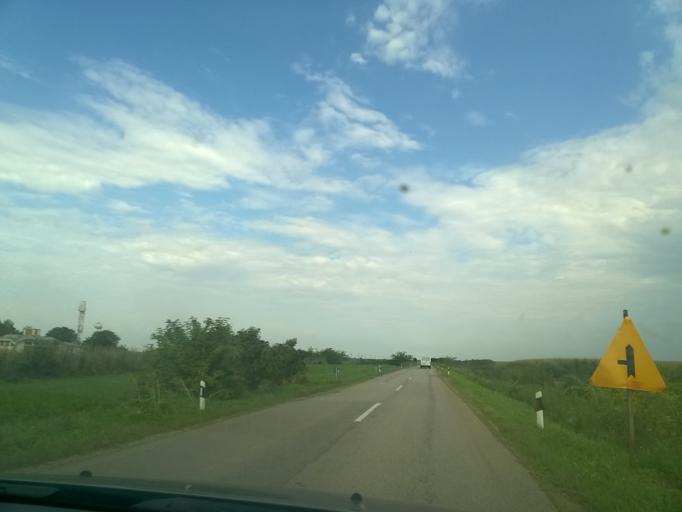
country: RS
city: Orlovat
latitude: 45.2750
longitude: 20.5306
